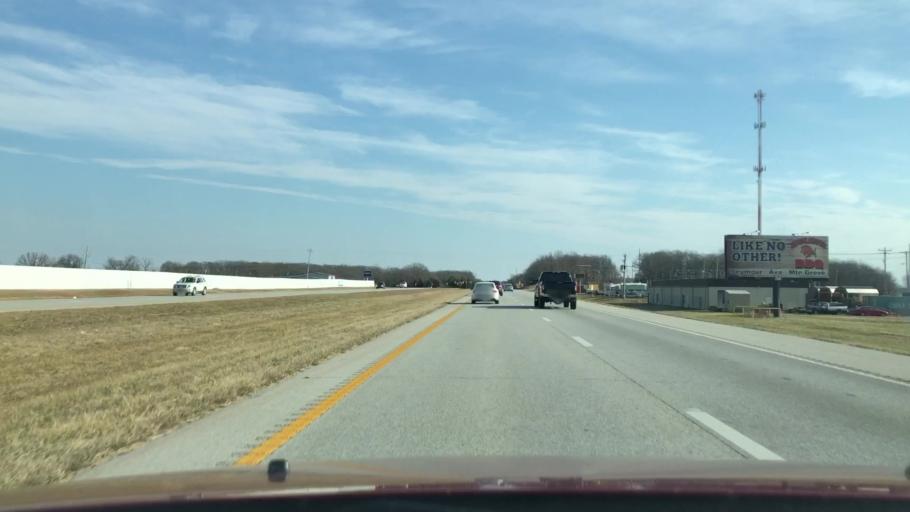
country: US
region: Missouri
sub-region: Webster County
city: Rogersville
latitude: 37.1178
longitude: -93.0176
